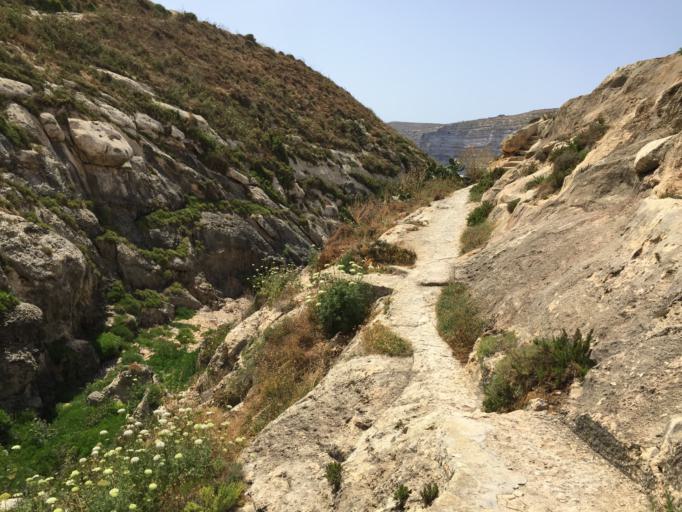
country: MT
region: Saint Lucia
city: Saint Lucia
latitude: 36.0272
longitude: 14.2166
